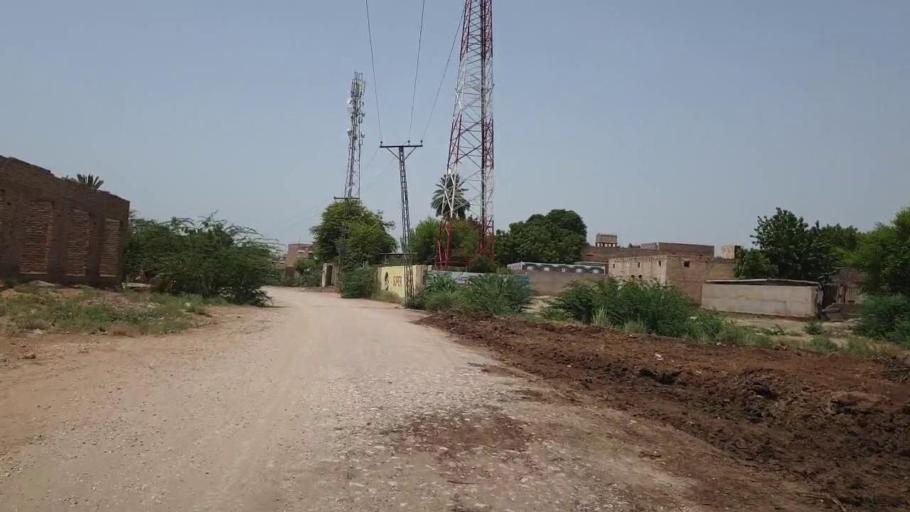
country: PK
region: Sindh
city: Daur
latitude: 26.3987
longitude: 68.4387
